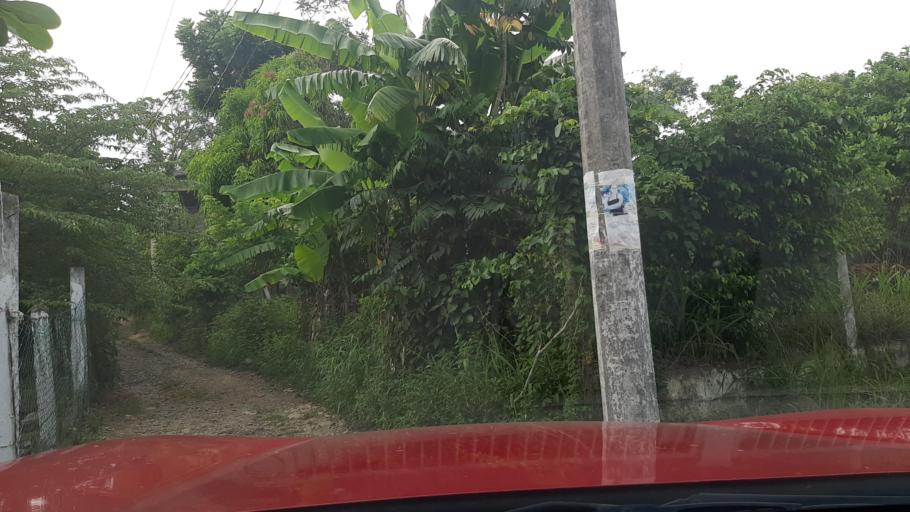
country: MX
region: Veracruz
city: Cazones de Herrera
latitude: 20.6730
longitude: -97.3260
